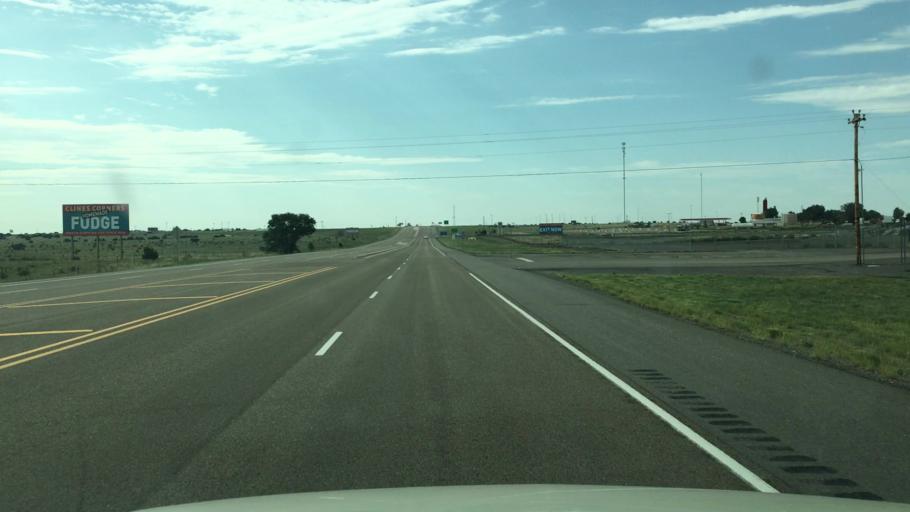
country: US
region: New Mexico
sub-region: Torrance County
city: Moriarty
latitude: 35.0163
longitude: -105.6688
